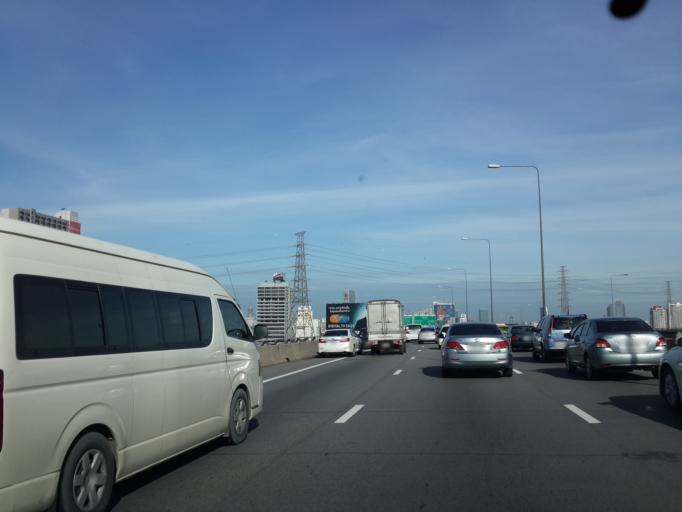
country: TH
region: Bangkok
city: Watthana
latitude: 13.7473
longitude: 100.6052
